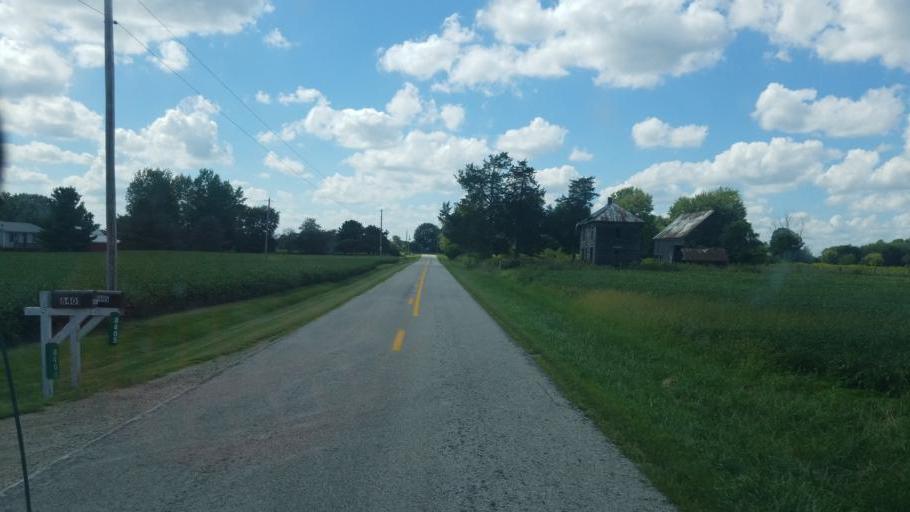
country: US
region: Ohio
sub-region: Union County
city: Richwood
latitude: 40.3502
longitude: -83.2273
